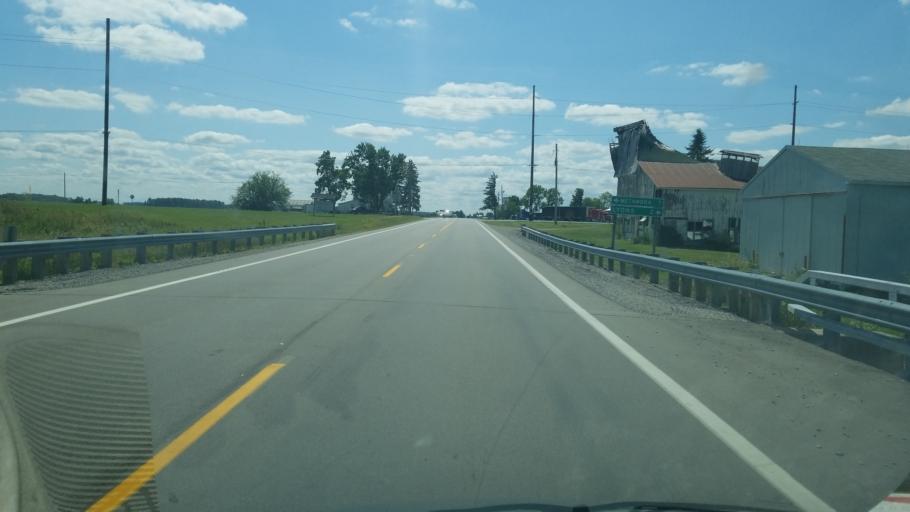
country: US
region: Ohio
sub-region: Fulton County
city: Delta
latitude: 41.7013
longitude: -84.0369
